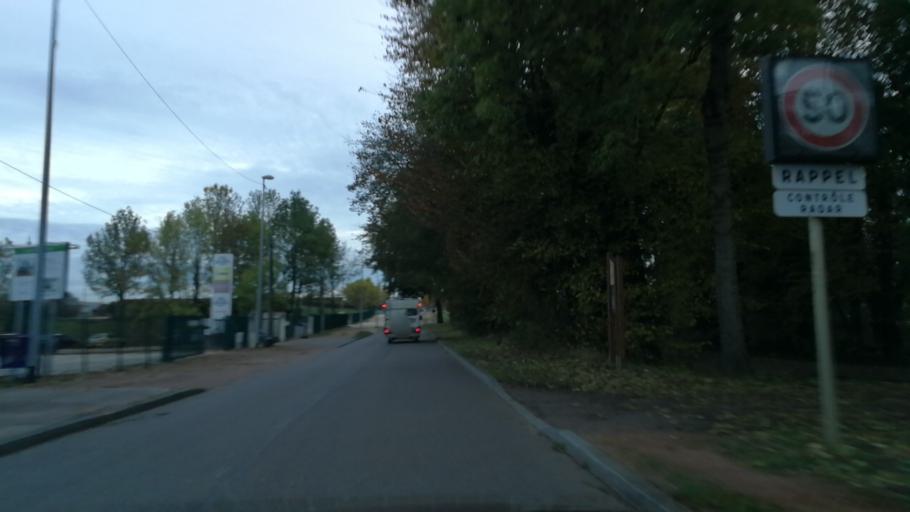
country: FR
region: Bourgogne
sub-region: Departement de la Cote-d'Or
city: Saint-Apollinaire
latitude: 47.3499
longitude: 5.0605
